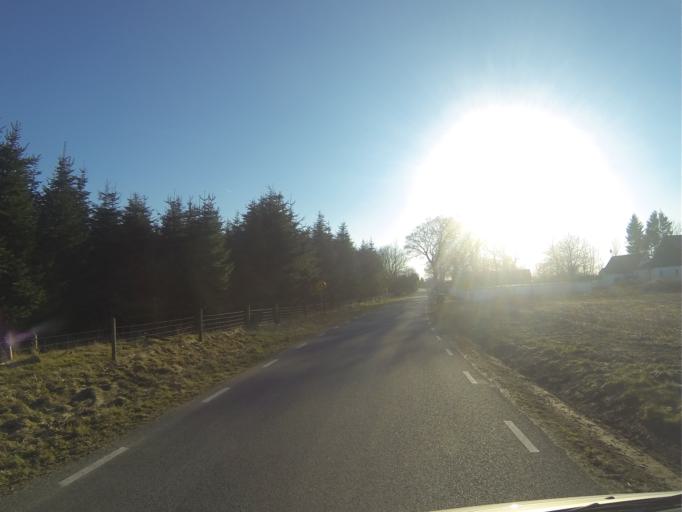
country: SE
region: Skane
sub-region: Hoors Kommun
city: Loberod
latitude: 55.7536
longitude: 13.4687
